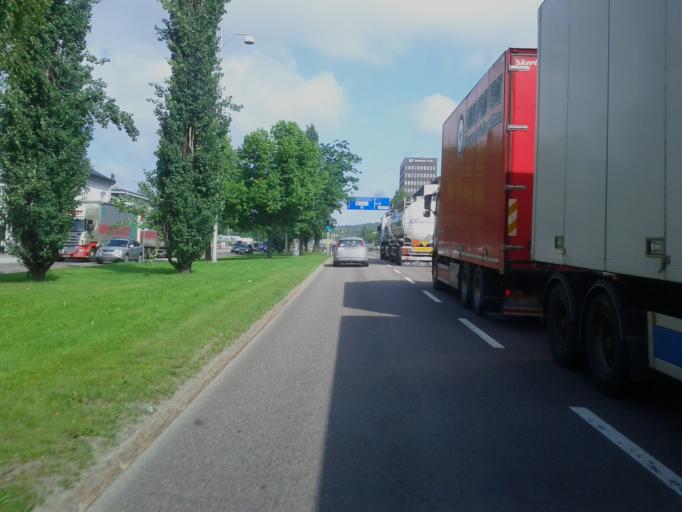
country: SE
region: Vaesterbotten
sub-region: Skelleftea Kommun
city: Skelleftea
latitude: 64.7496
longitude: 20.9607
